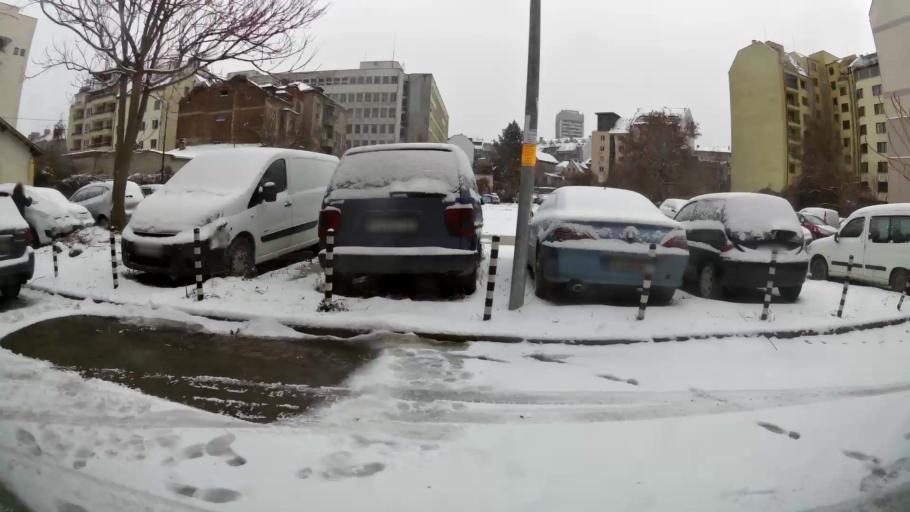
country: BG
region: Sofia-Capital
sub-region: Stolichna Obshtina
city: Sofia
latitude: 42.6972
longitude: 23.3112
